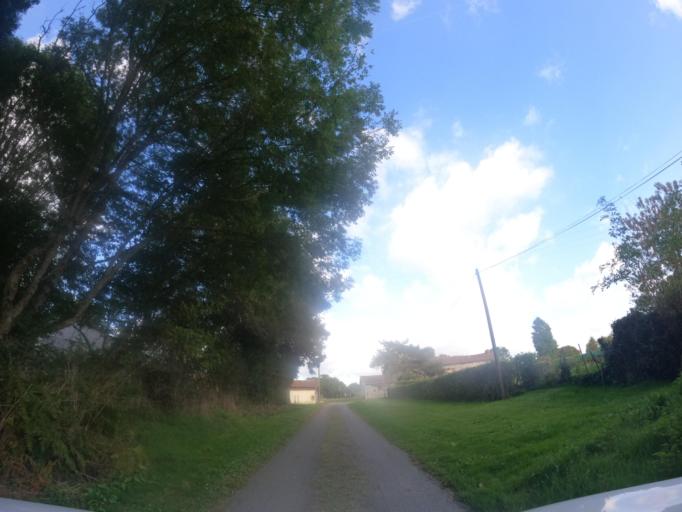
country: FR
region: Poitou-Charentes
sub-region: Departement des Deux-Sevres
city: Courlay
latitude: 46.7998
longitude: -0.6060
